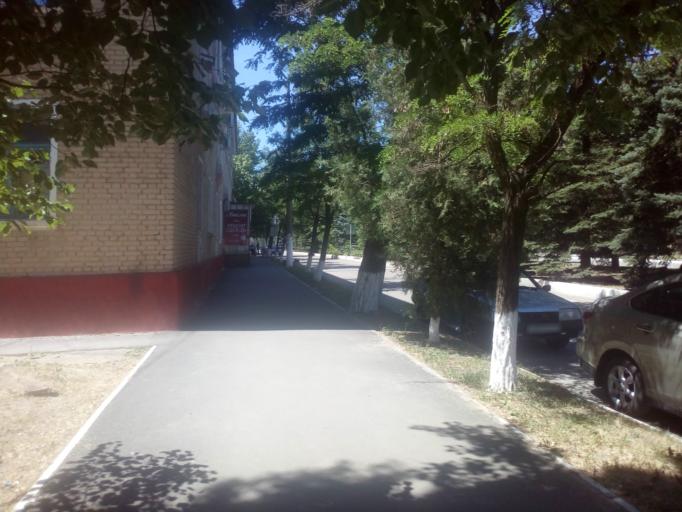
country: RU
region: Rostov
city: Sholokhovskiy
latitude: 48.2824
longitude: 41.0446
